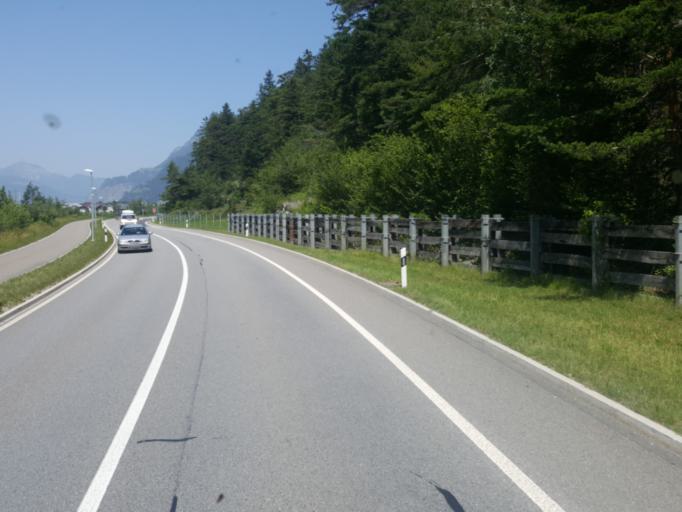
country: CH
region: Uri
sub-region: Uri
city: Erstfeld
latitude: 46.8409
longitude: 8.6452
